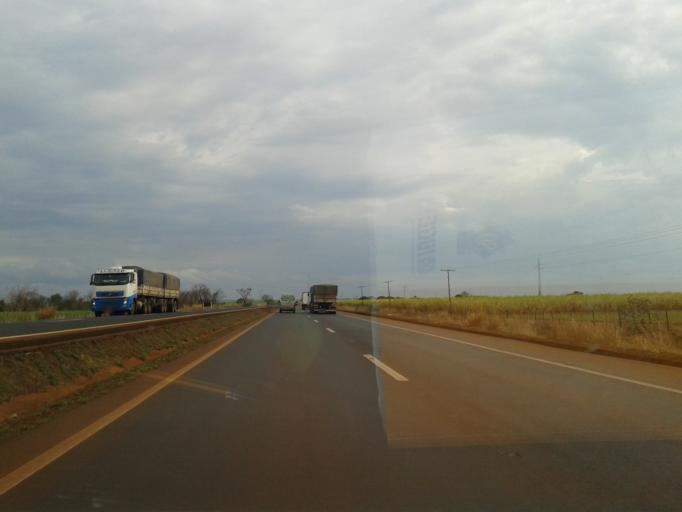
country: BR
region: Goias
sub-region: Itumbiara
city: Itumbiara
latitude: -18.4898
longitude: -49.1888
